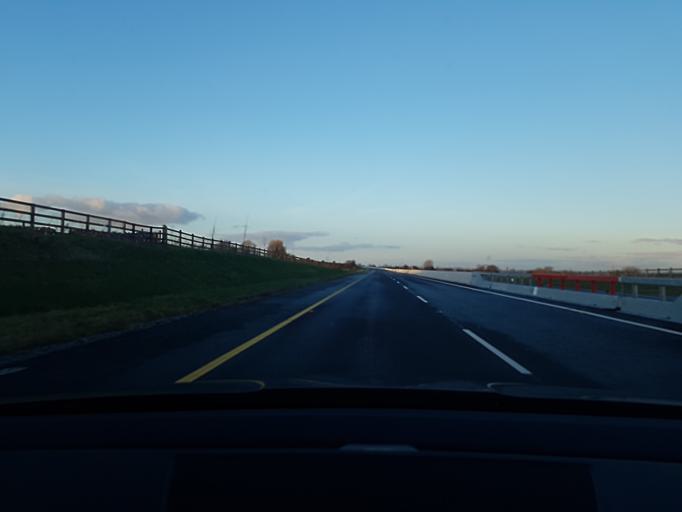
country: IE
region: Connaught
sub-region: County Galway
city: Tuam
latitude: 53.4802
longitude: -8.8636
